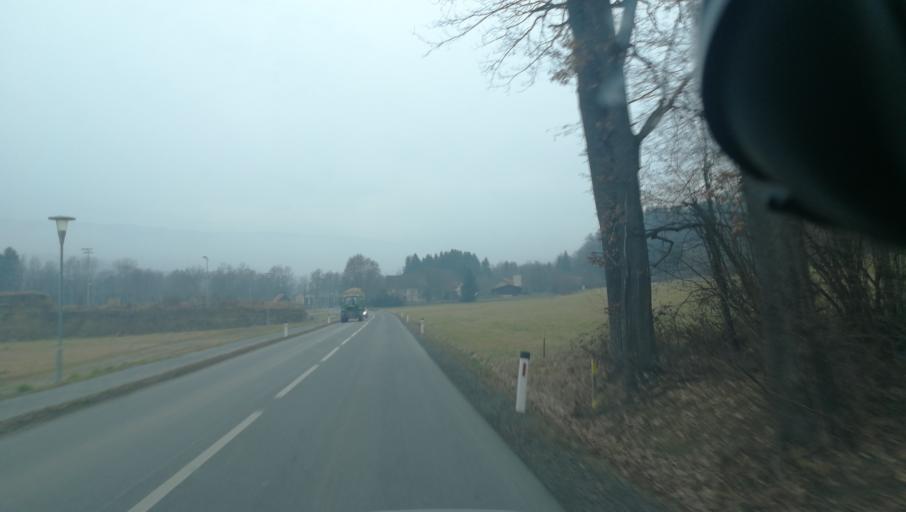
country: AT
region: Styria
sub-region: Politischer Bezirk Deutschlandsberg
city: Stainz
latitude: 46.8995
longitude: 15.2506
